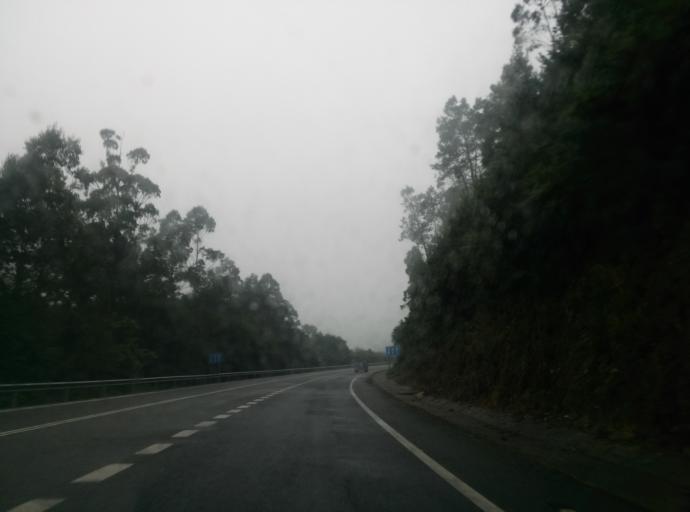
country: ES
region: Galicia
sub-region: Provincia de Lugo
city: Muras
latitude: 43.5393
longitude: -7.6574
